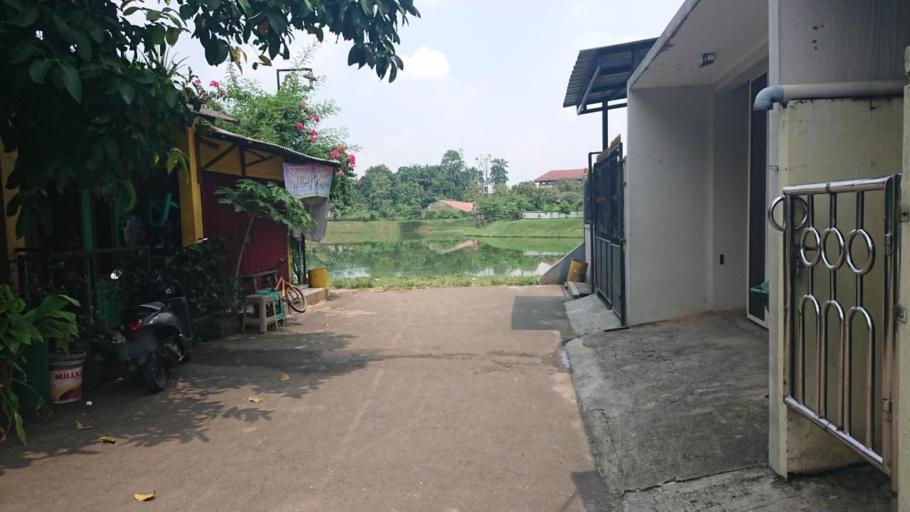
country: ID
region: Banten
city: South Tangerang
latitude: -6.2417
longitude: 106.7557
